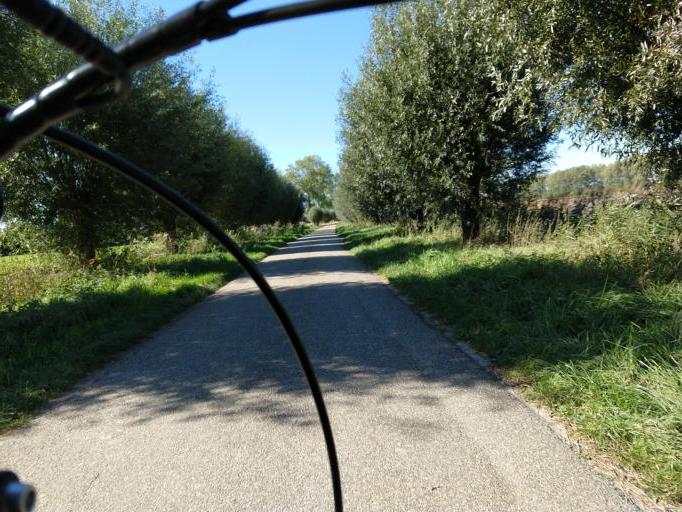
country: NL
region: Zeeland
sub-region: Gemeente Goes
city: Goes
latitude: 51.4411
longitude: 3.8483
